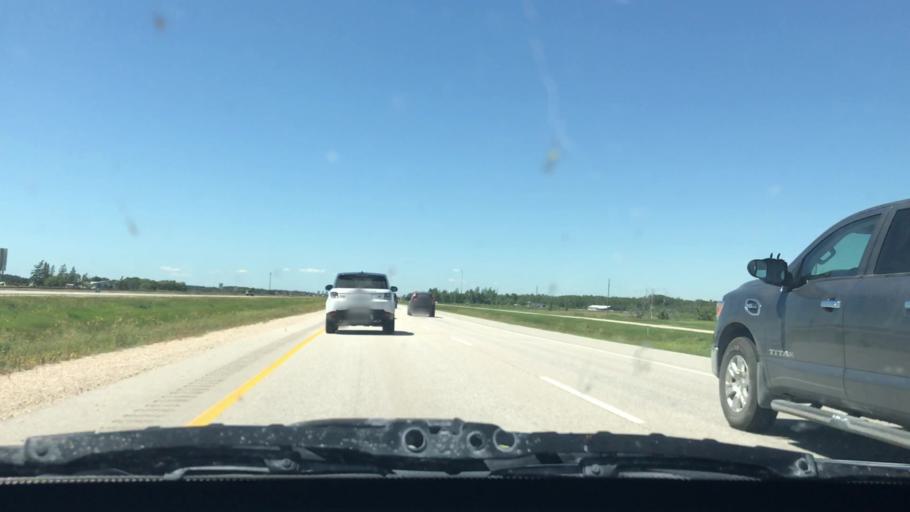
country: CA
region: Manitoba
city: Niverville
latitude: 49.8115
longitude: -96.9140
